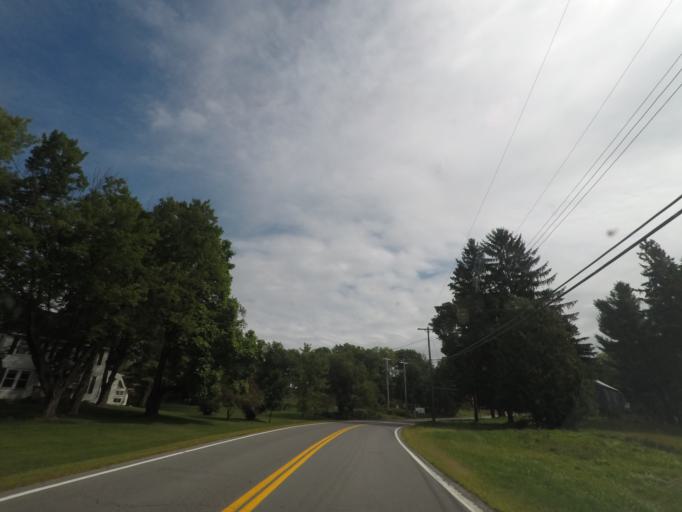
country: US
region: New York
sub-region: Rensselaer County
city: Nassau
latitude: 42.5508
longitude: -73.6174
